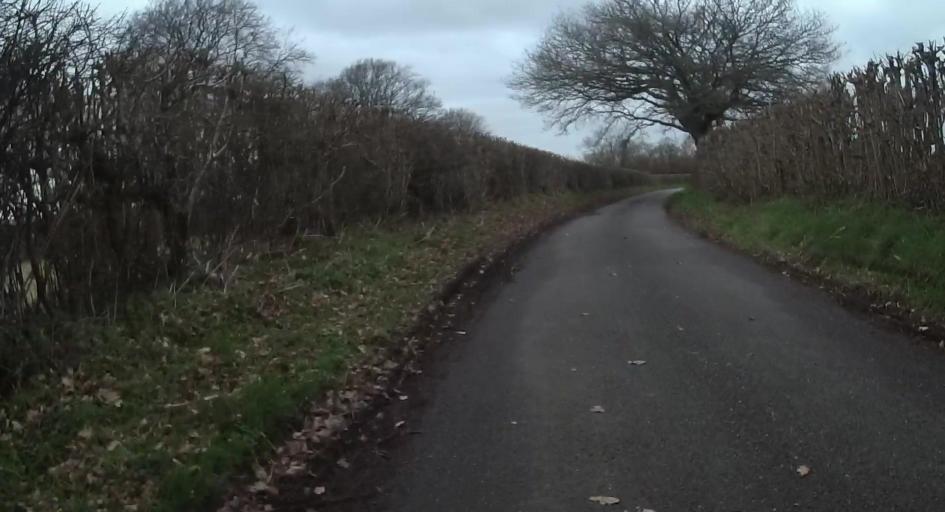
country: GB
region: England
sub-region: Hampshire
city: Four Marks
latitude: 51.1343
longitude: -1.0407
